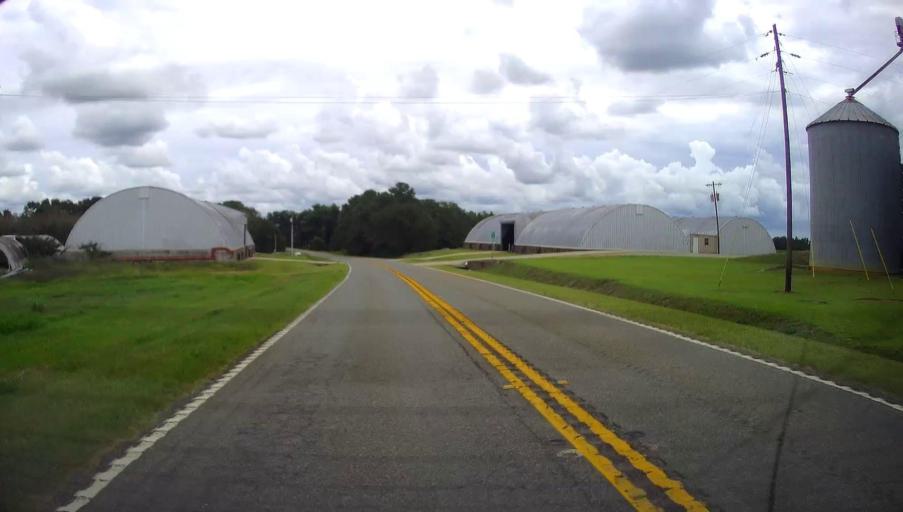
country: US
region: Georgia
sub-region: Dooly County
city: Unadilla
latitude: 32.2602
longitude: -83.8045
